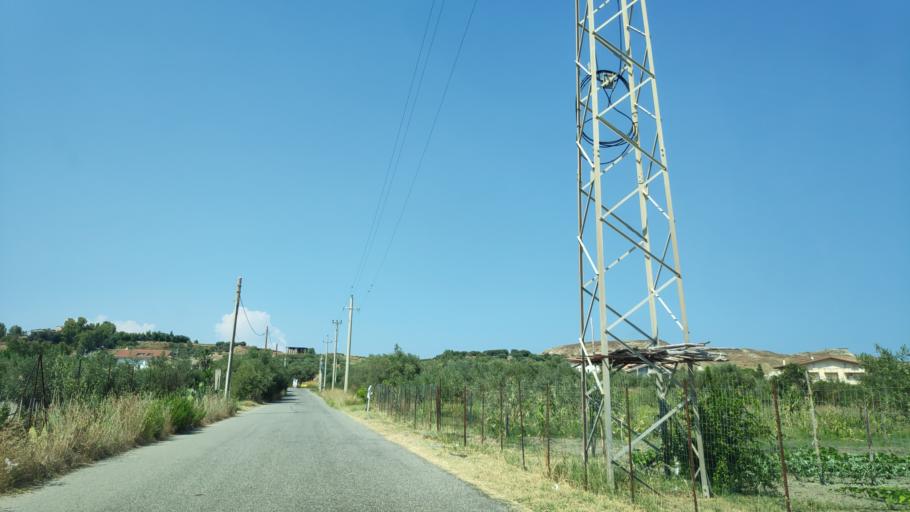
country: IT
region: Calabria
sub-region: Provincia di Reggio Calabria
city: Monasterace Marina
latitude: 38.4255
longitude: 16.5436
